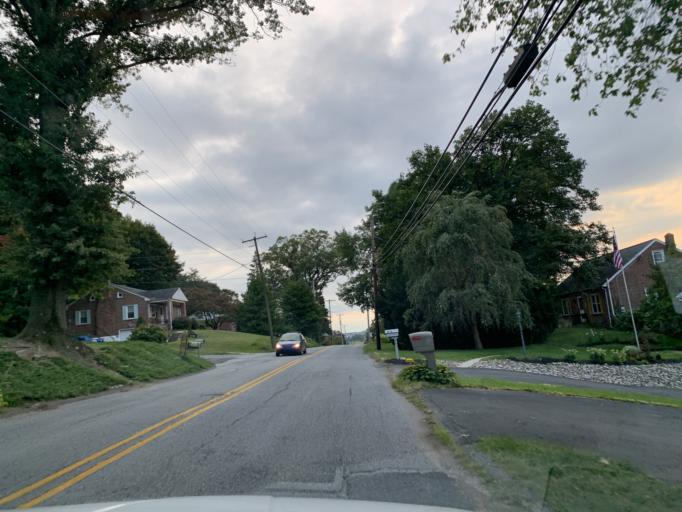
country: US
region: Pennsylvania
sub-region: York County
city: Emigsville
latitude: 40.0024
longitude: -76.7282
